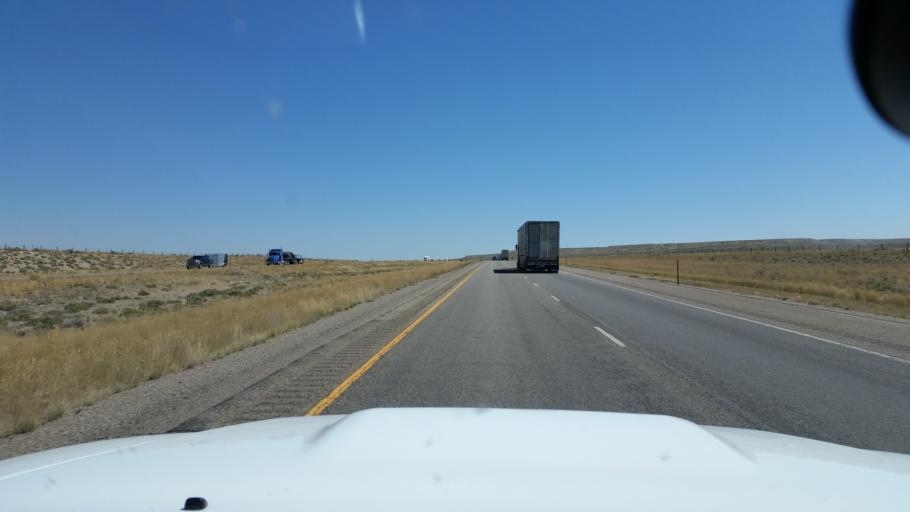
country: US
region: Wyoming
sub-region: Sweetwater County
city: Green River
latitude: 41.5449
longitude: -109.6233
